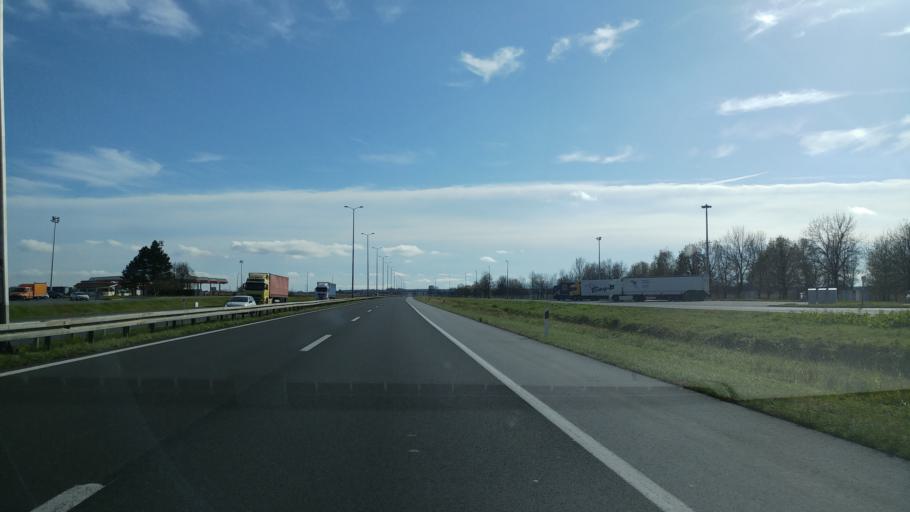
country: HR
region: Sisacko-Moslavacka
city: Lipovljani
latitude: 45.4030
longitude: 16.8595
